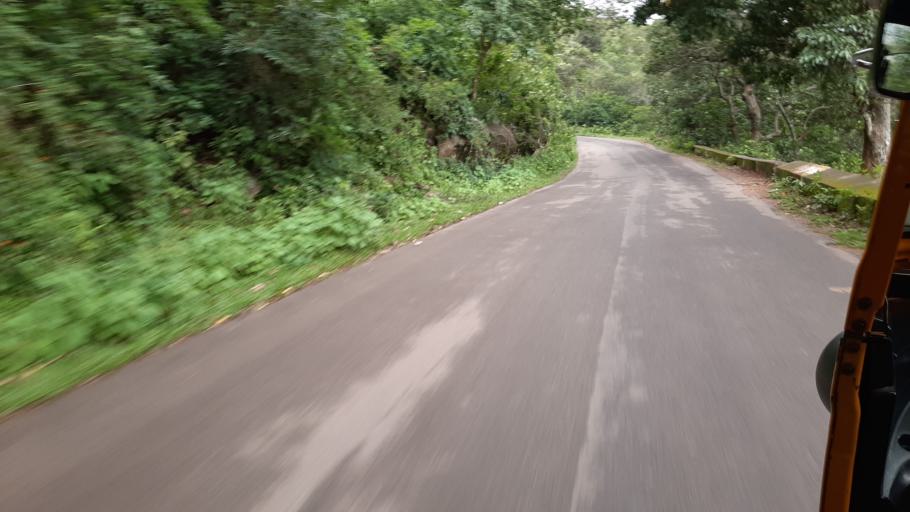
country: IN
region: Andhra Pradesh
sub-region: Vizianagaram District
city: Salur
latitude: 18.2412
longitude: 83.0163
